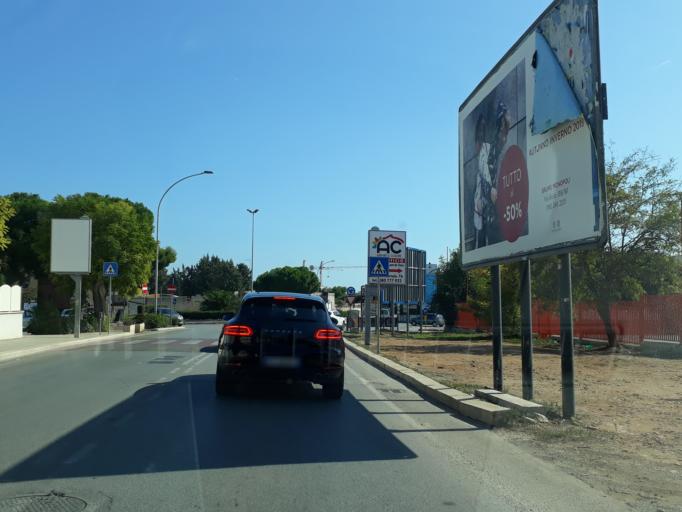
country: IT
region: Apulia
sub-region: Provincia di Bari
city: Monopoli
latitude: 40.9430
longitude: 17.3027
